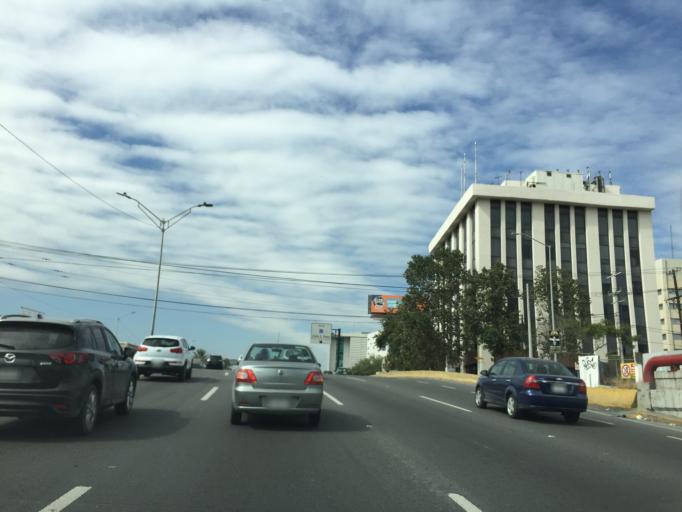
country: MX
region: Nuevo Leon
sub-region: Monterrey
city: Monterrey
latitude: 25.6657
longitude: -100.3210
